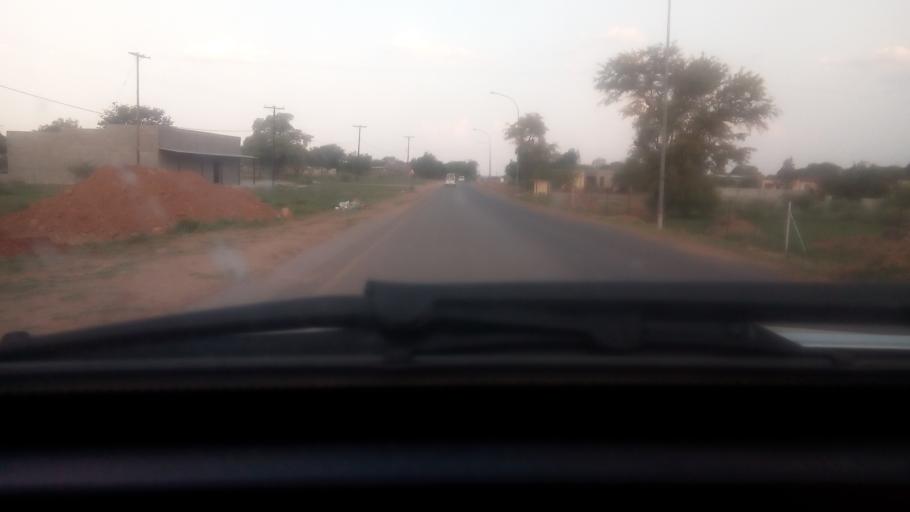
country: BW
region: Kgatleng
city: Bokaa
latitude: -24.4287
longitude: 26.0210
